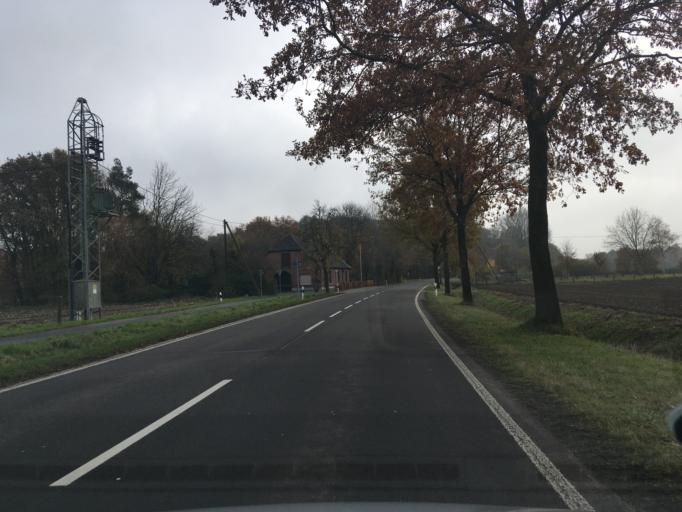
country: DE
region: North Rhine-Westphalia
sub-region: Regierungsbezirk Munster
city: Sudlohn
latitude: 51.9296
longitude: 6.8823
